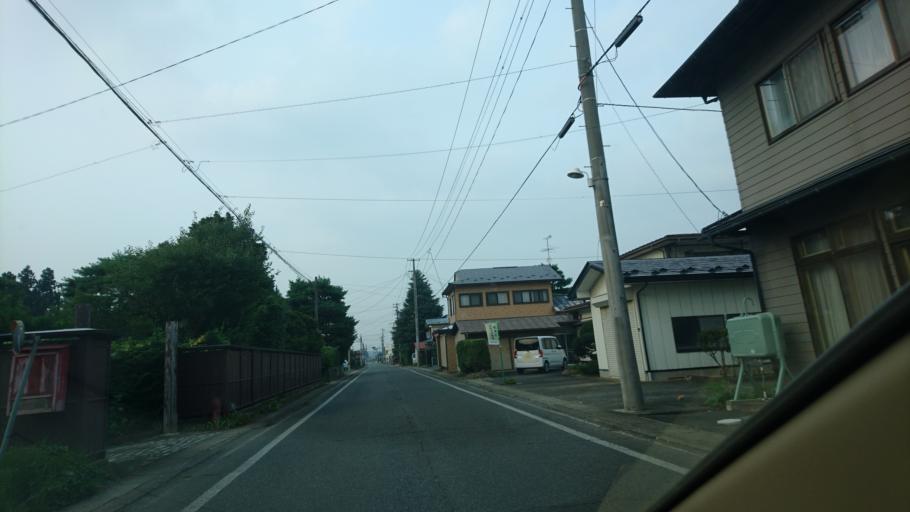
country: JP
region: Iwate
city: Mizusawa
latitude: 39.1743
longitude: 141.1546
